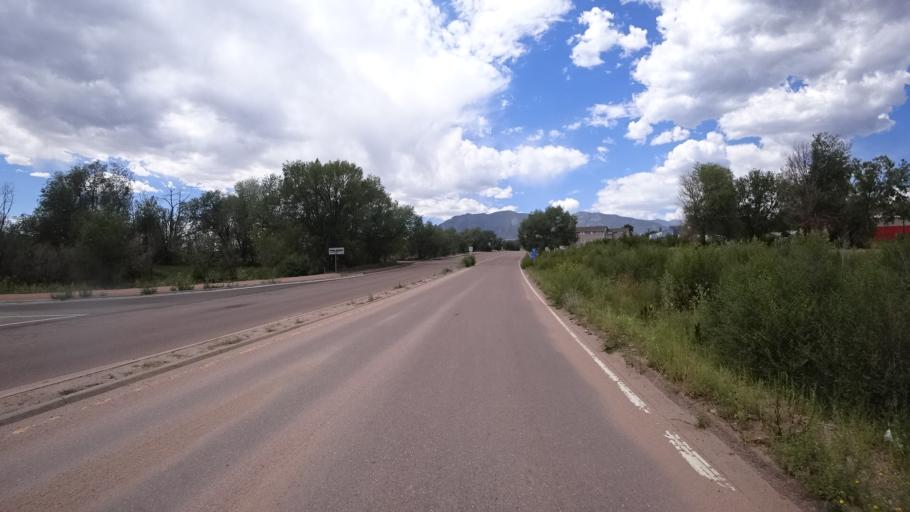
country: US
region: Colorado
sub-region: El Paso County
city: Stratmoor
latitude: 38.7770
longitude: -104.7852
